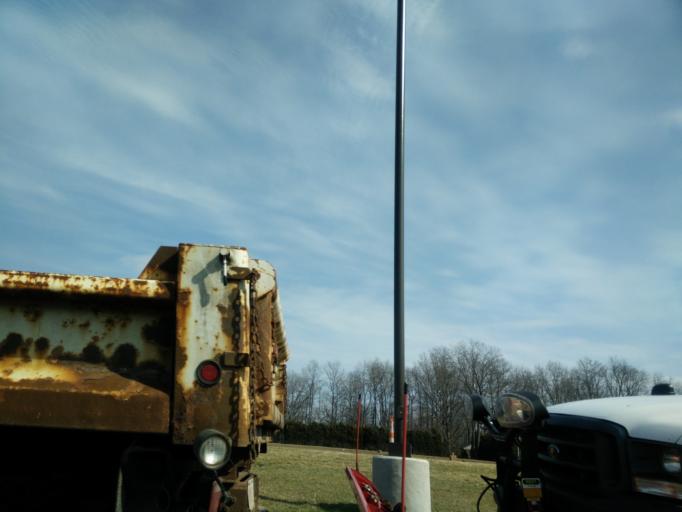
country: US
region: Ohio
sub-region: Cuyahoga County
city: University Heights
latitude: 41.4996
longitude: -81.5276
